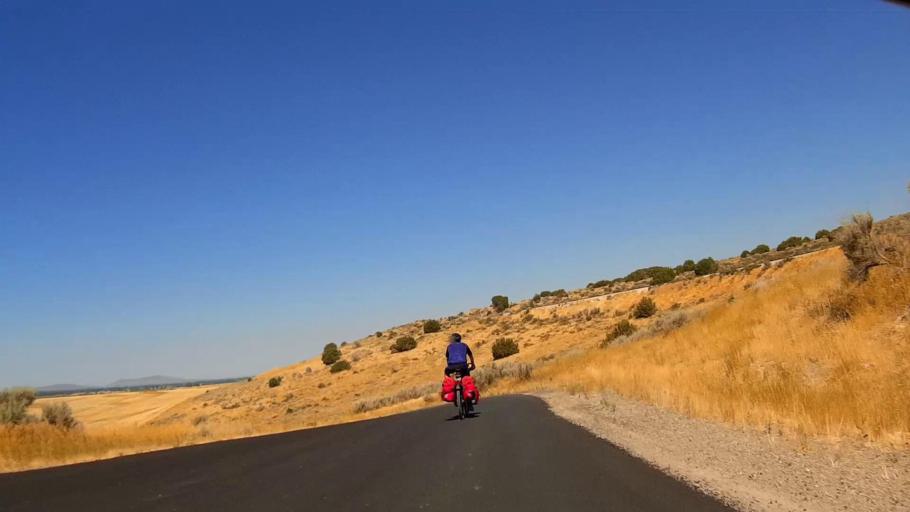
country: US
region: Idaho
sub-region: Madison County
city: Rexburg
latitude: 43.7176
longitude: -111.7489
